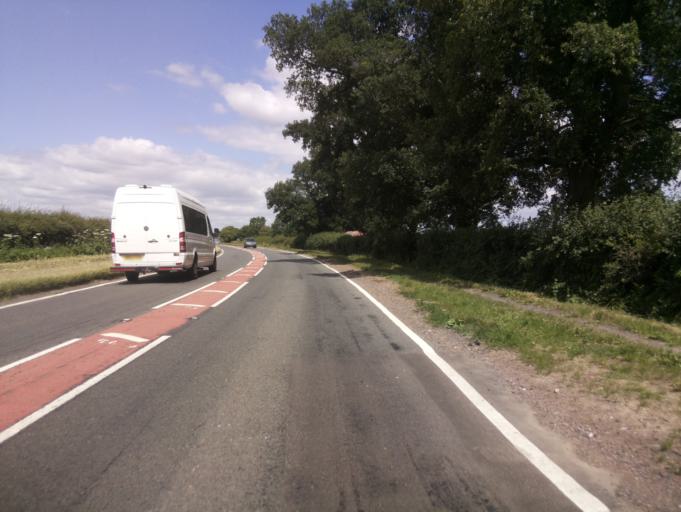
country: GB
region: England
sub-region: Buckinghamshire
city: Aylesbury
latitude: 51.8491
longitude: -0.8258
